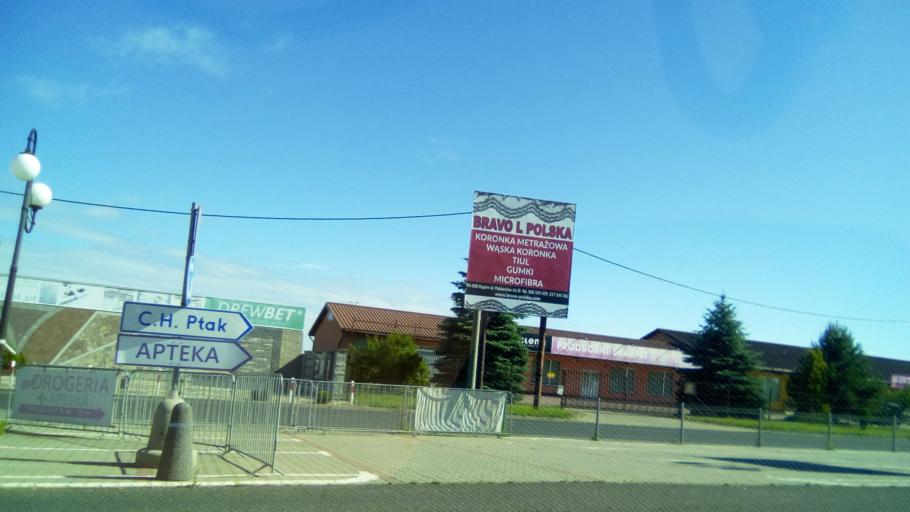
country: PL
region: Lodz Voivodeship
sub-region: Powiat lodzki wschodni
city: Rzgow
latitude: 51.6510
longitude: 19.4869
